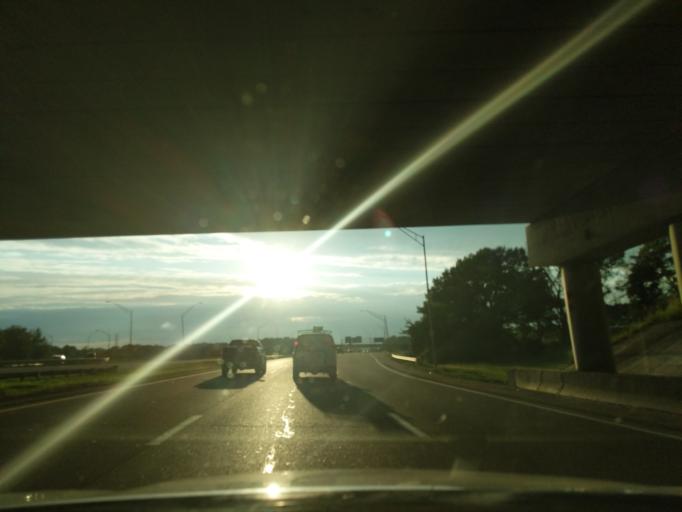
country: US
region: Tennessee
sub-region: Shelby County
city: New South Memphis
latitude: 35.0716
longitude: -90.0208
